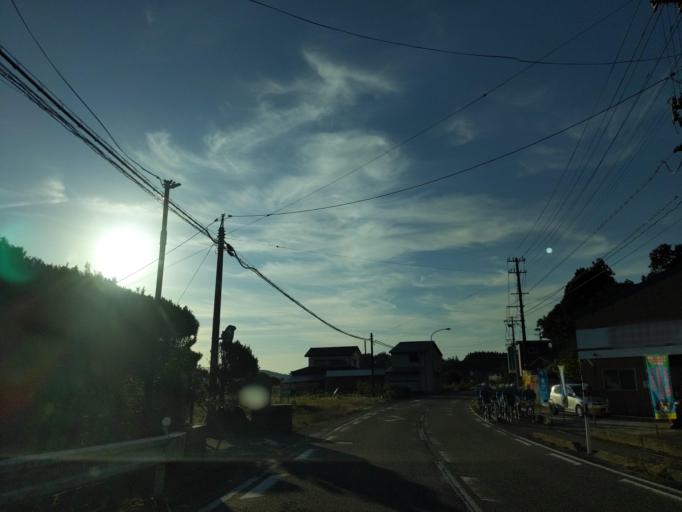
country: JP
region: Niigata
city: Nagaoka
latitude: 37.5785
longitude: 138.7668
